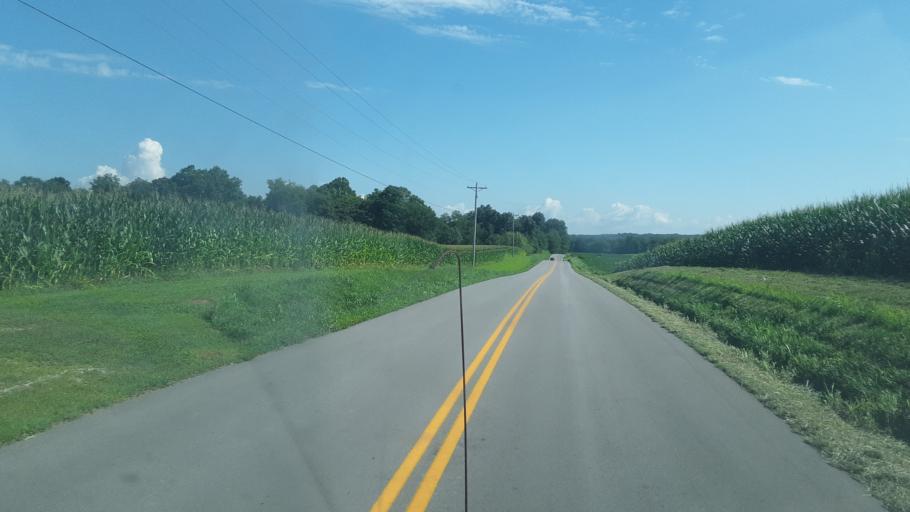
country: US
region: Kentucky
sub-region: Todd County
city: Elkton
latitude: 36.7482
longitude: -87.2251
